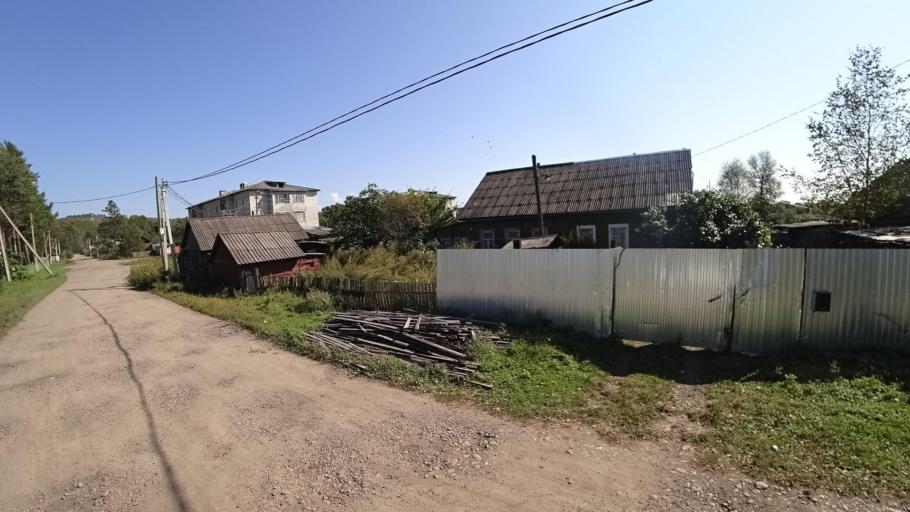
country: RU
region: Jewish Autonomous Oblast
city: Bira
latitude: 48.9966
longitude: 132.4548
